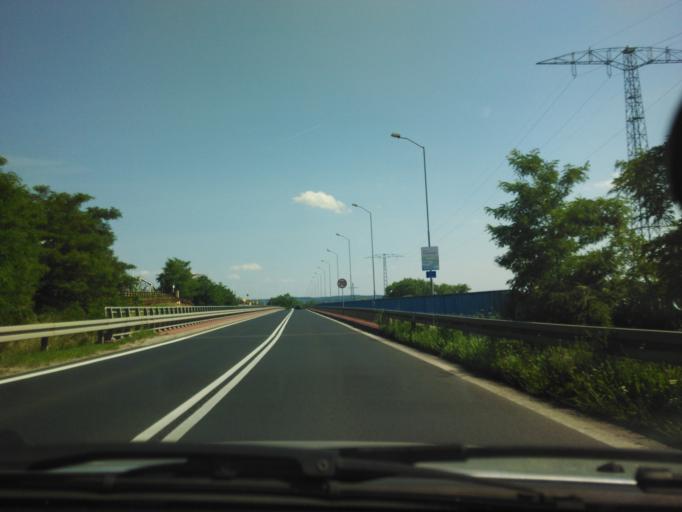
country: PL
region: West Pomeranian Voivodeship
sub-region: Szczecin
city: Szczecin
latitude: 53.3835
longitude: 14.5331
